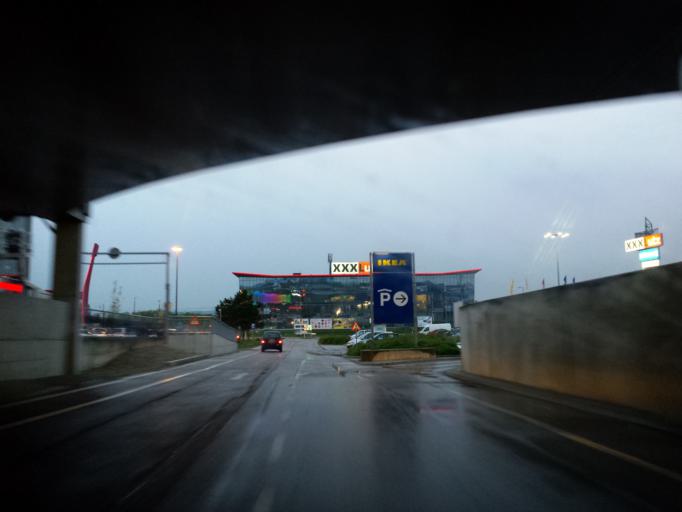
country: AT
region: Lower Austria
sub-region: Politischer Bezirk Modling
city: Wiener Neudorf
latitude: 48.1050
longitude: 16.3174
